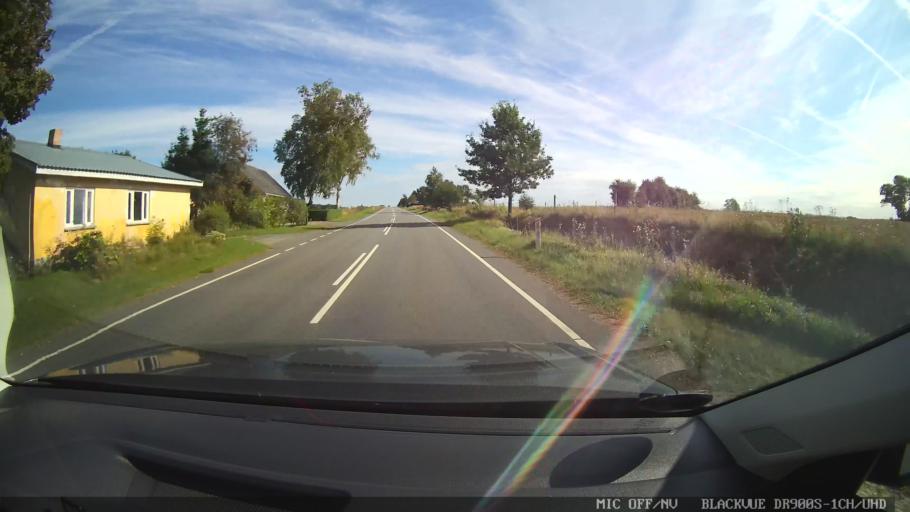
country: DK
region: North Denmark
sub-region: Rebild Kommune
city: Skorping
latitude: 56.7723
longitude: 9.9979
